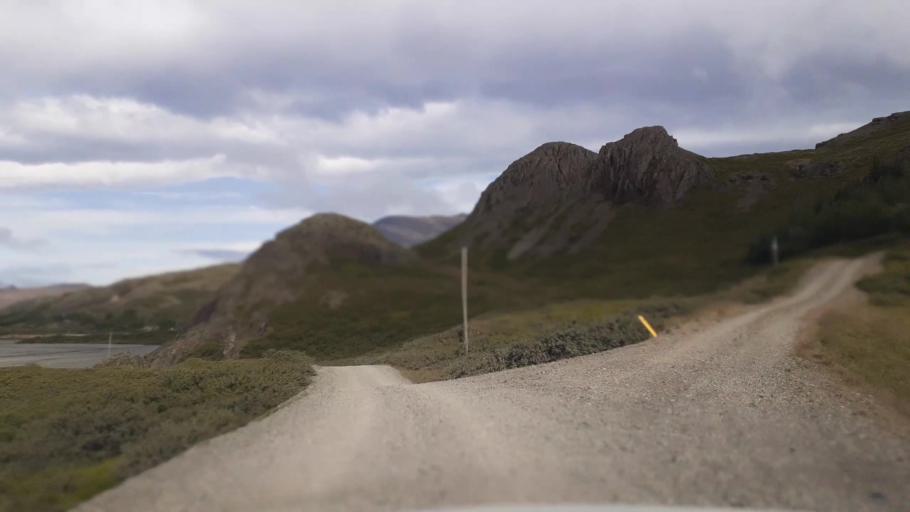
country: IS
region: East
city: Hoefn
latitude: 64.4297
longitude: -14.8866
